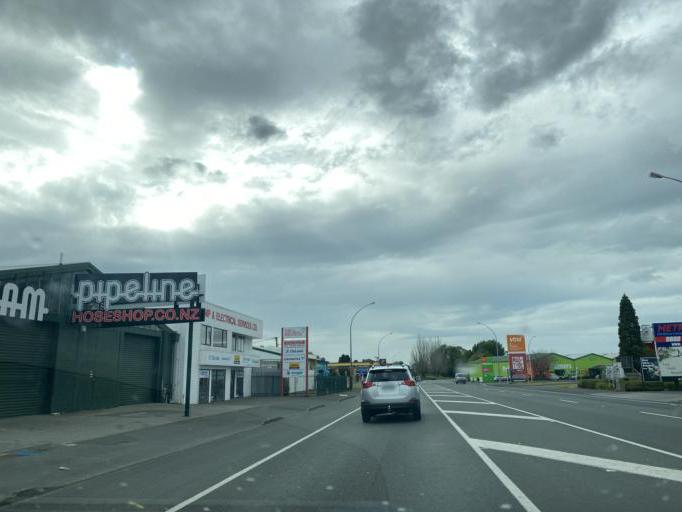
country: NZ
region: Waikato
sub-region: Hamilton City
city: Hamilton
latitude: -37.7872
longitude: 175.2574
